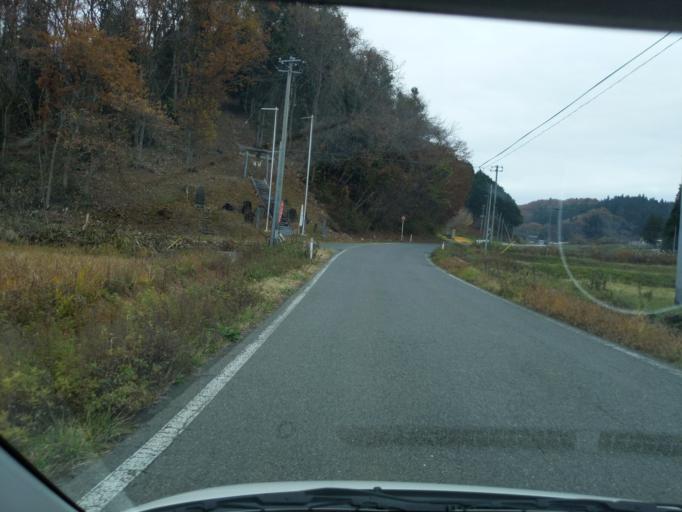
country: JP
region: Iwate
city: Kitakami
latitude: 39.2801
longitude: 141.1749
